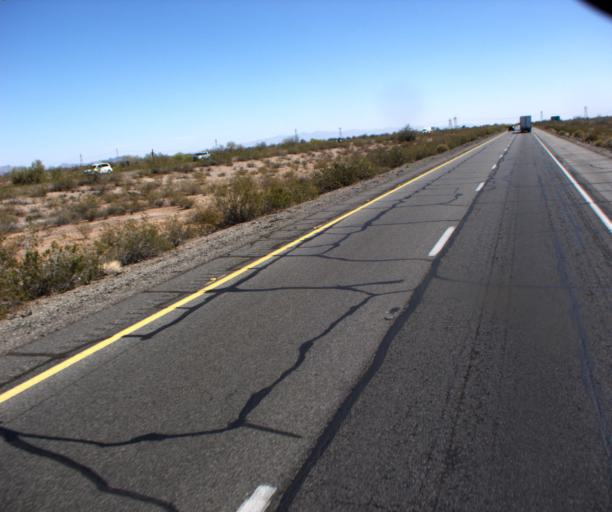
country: US
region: Arizona
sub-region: Maricopa County
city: Buckeye
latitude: 33.5176
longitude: -113.0536
